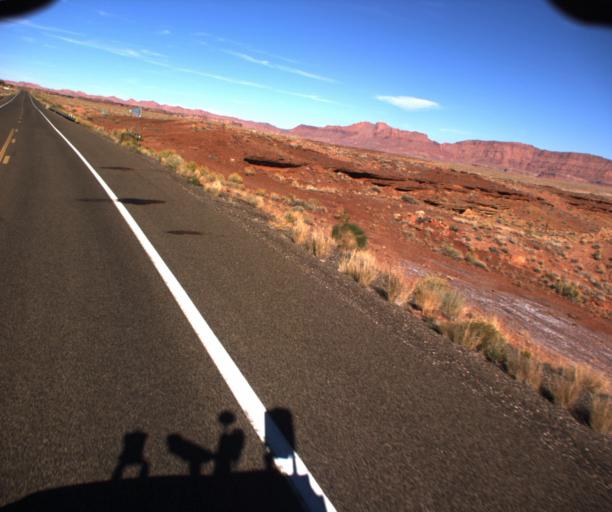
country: US
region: Arizona
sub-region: Coconino County
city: Page
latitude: 36.7815
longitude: -111.6888
